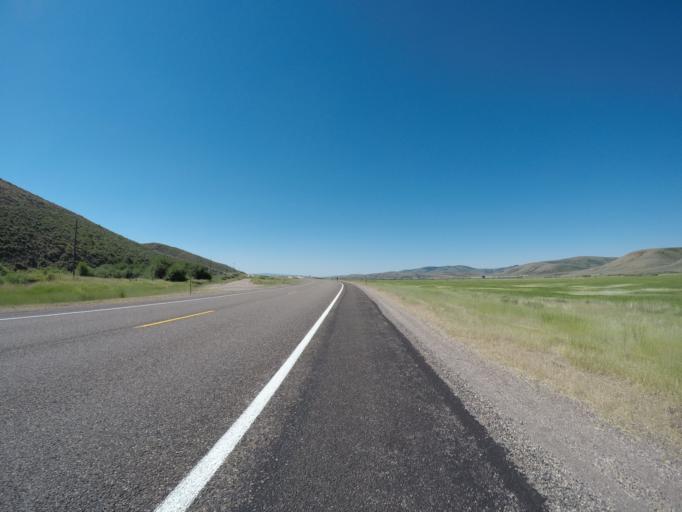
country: US
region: Idaho
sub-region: Bear Lake County
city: Montpelier
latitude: 42.3896
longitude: -111.0532
